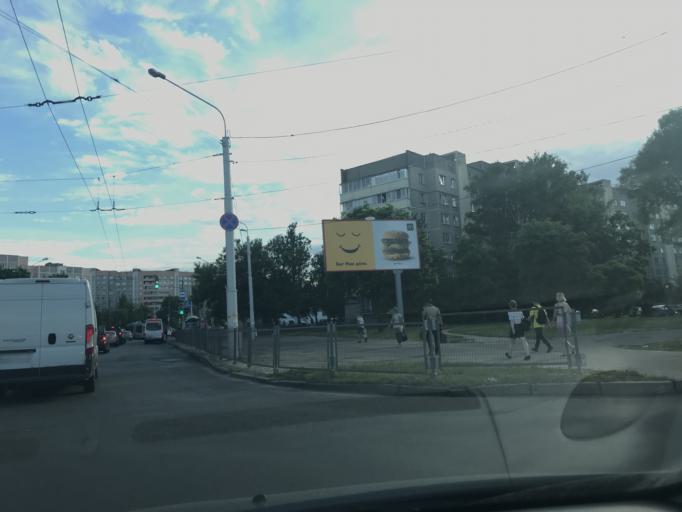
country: BY
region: Minsk
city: Bal'shavik
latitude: 53.9621
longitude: 27.6182
